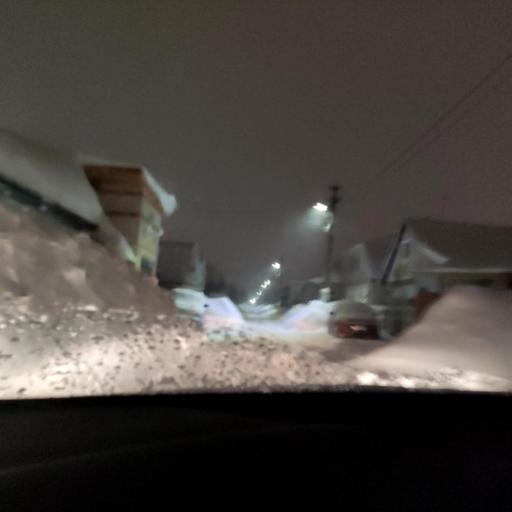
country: RU
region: Tatarstan
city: Staroye Arakchino
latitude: 55.8778
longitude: 49.0302
